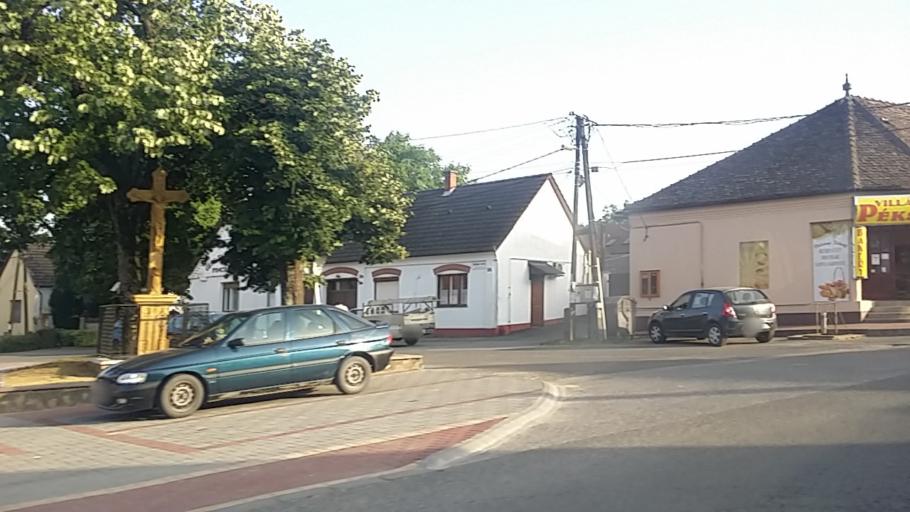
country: HU
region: Baranya
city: Villany
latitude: 45.8668
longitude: 18.4512
